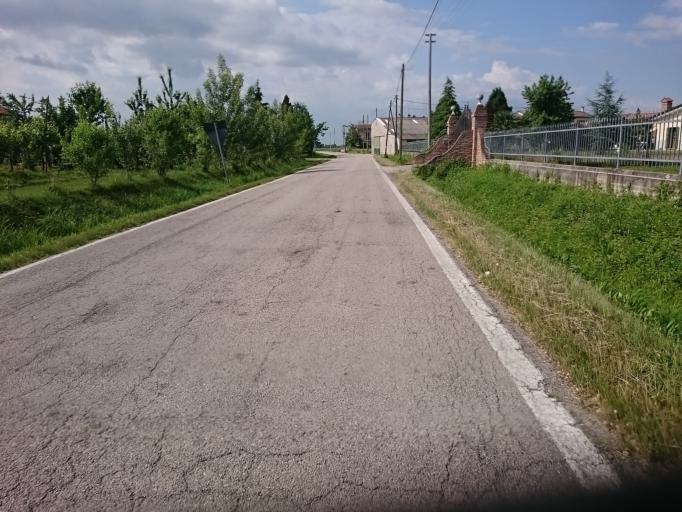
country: IT
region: Veneto
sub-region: Provincia di Padova
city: Casale di Scodosia
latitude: 45.1950
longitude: 11.4912
